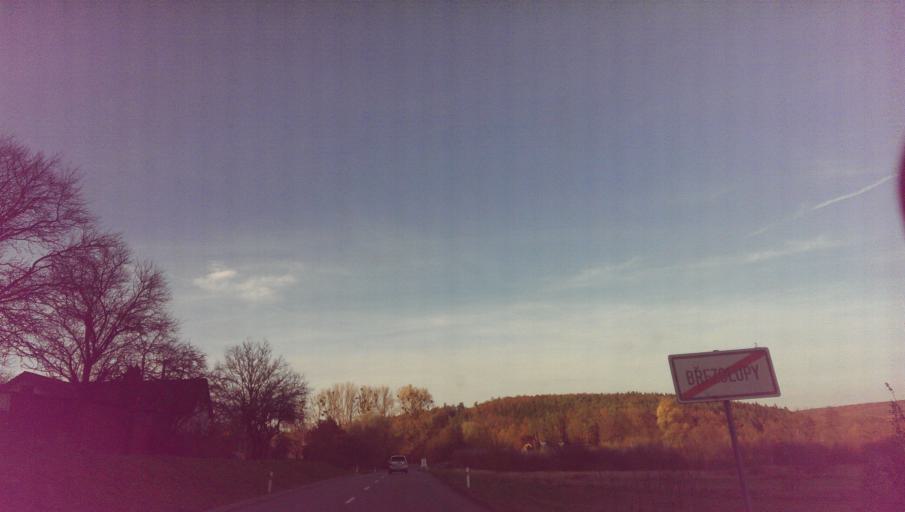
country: CZ
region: Zlin
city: Brezolupy
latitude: 49.1279
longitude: 17.5892
